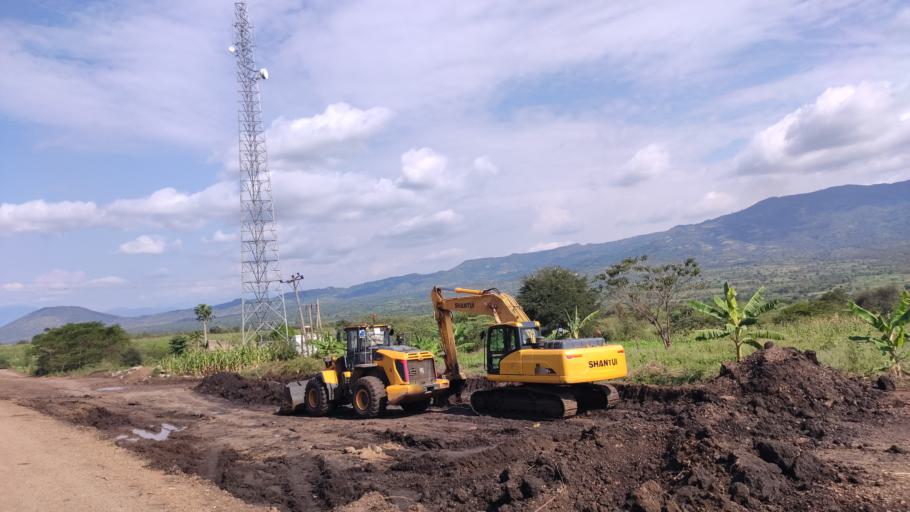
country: ET
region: Southern Nations, Nationalities, and People's Region
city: Felege Neway
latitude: 6.3968
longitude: 37.1100
